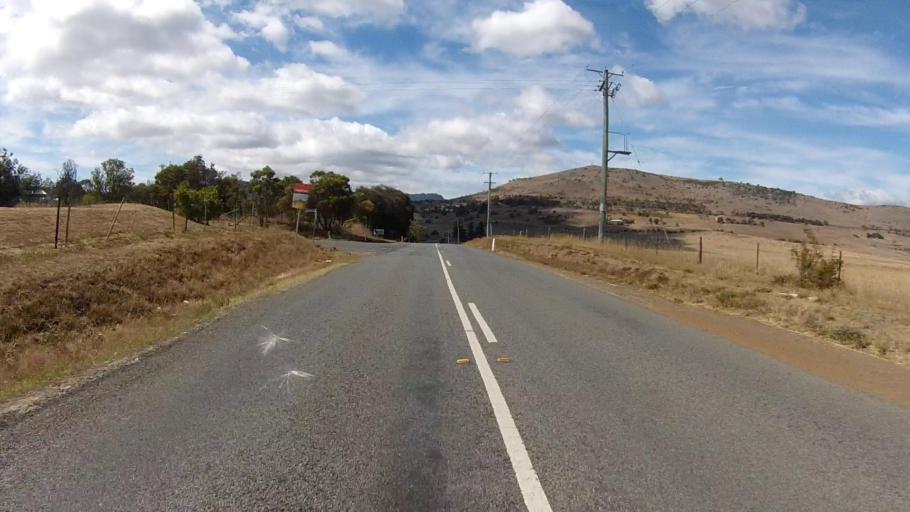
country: AU
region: Tasmania
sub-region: Brighton
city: Bridgewater
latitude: -42.7179
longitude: 147.2771
